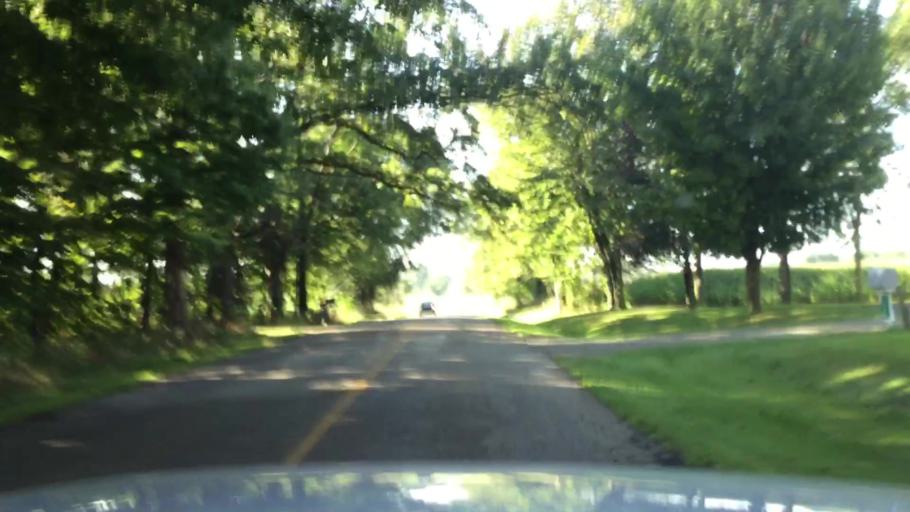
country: US
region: Michigan
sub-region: Lenawee County
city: Hudson
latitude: 41.9208
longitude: -84.4205
